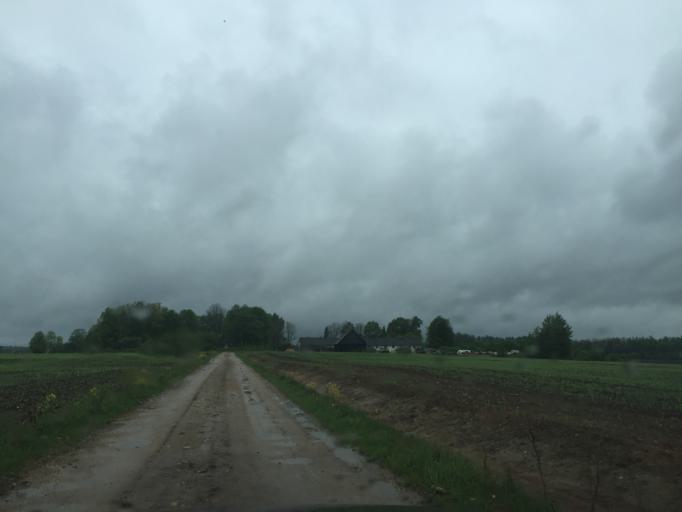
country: LV
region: Ogre
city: Jumprava
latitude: 56.6617
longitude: 25.0085
